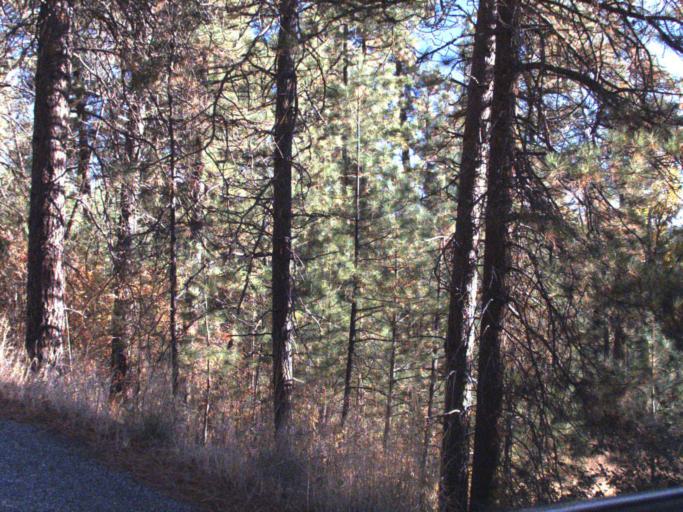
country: US
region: Washington
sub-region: Okanogan County
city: Coulee Dam
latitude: 48.0677
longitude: -118.6733
